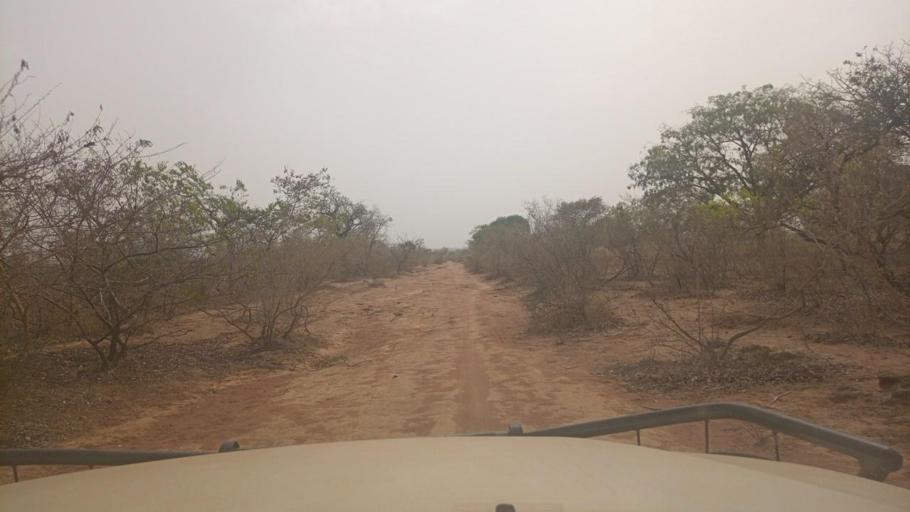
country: BF
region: Boucle du Mouhoun
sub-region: Province des Banwa
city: Salanso
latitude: 12.1661
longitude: -4.2353
